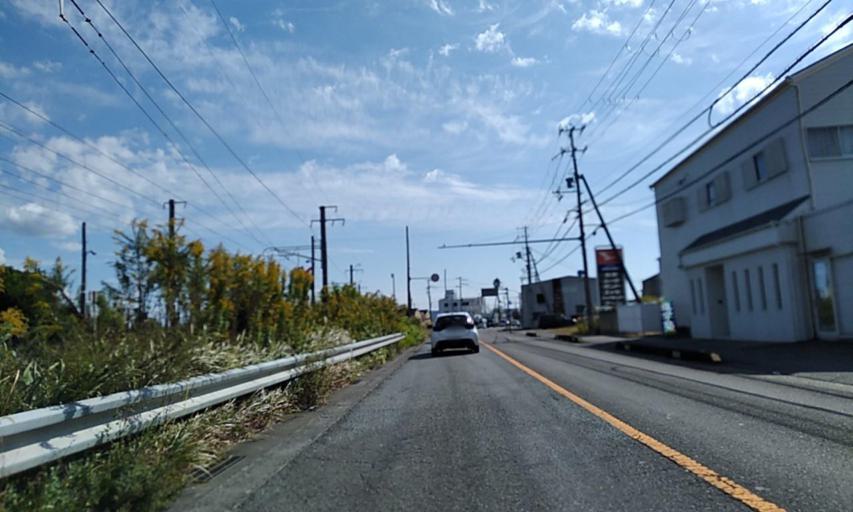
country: JP
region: Wakayama
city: Gobo
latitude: 33.9093
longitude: 135.1503
